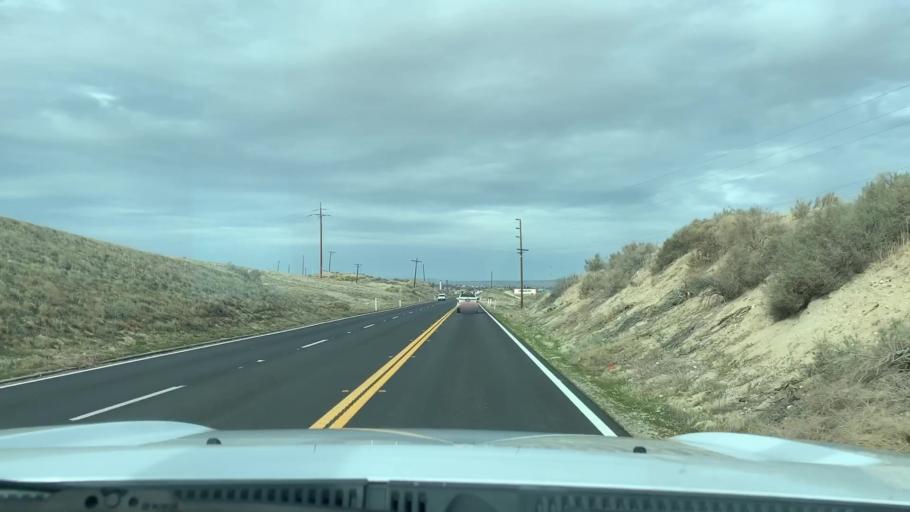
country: US
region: California
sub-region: Kern County
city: South Taft
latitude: 35.1214
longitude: -119.4356
